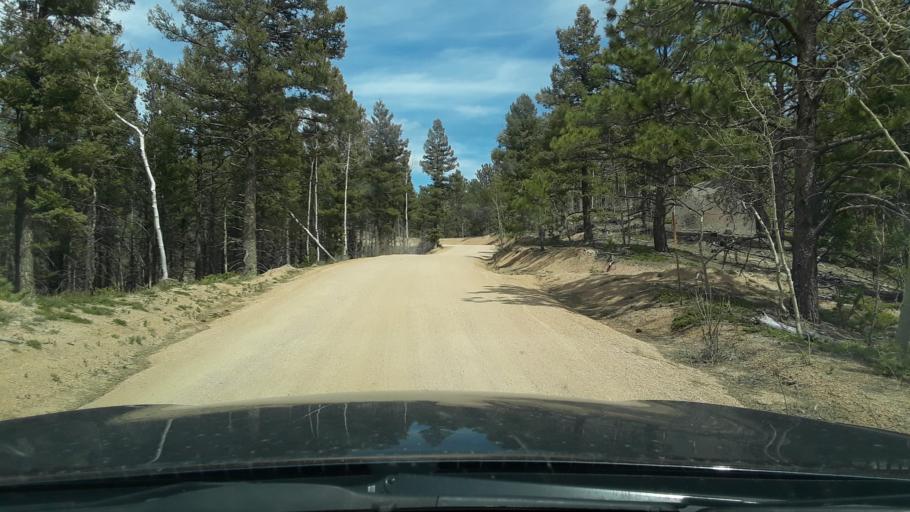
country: US
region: Colorado
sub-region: El Paso County
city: Palmer Lake
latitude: 39.0684
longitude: -104.9613
